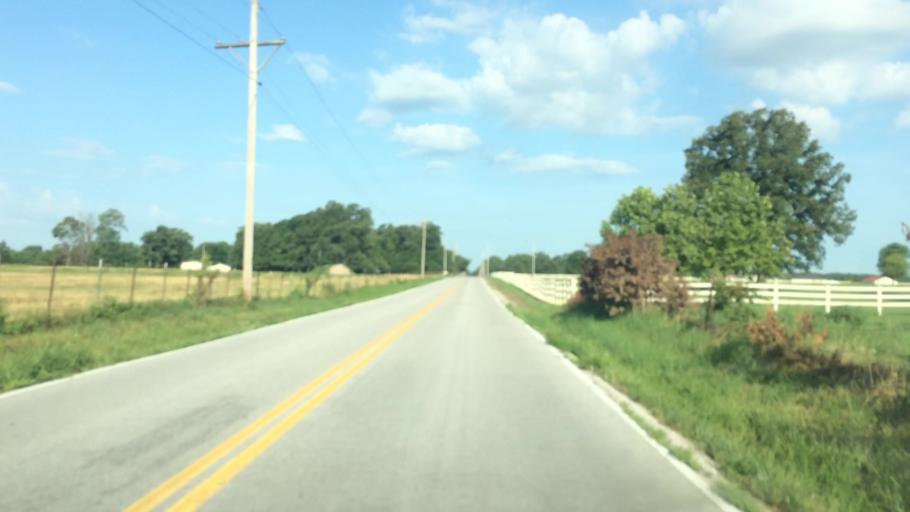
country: US
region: Missouri
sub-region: Greene County
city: Strafford
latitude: 37.2714
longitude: -93.1587
